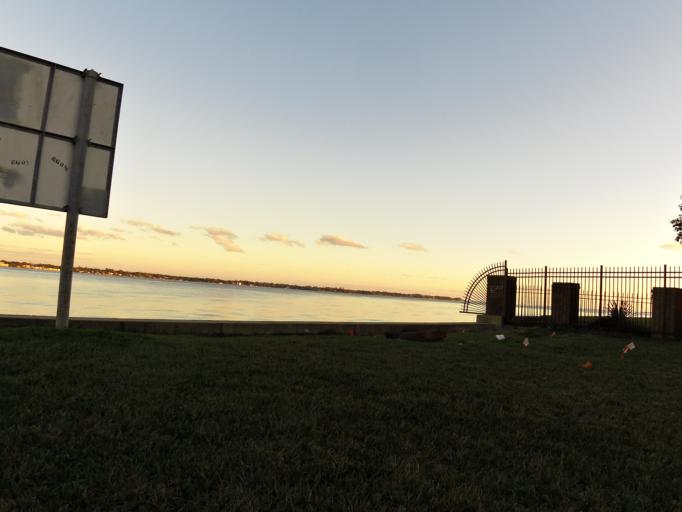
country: US
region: Florida
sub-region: Duval County
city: Jacksonville
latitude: 30.3123
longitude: -81.6767
